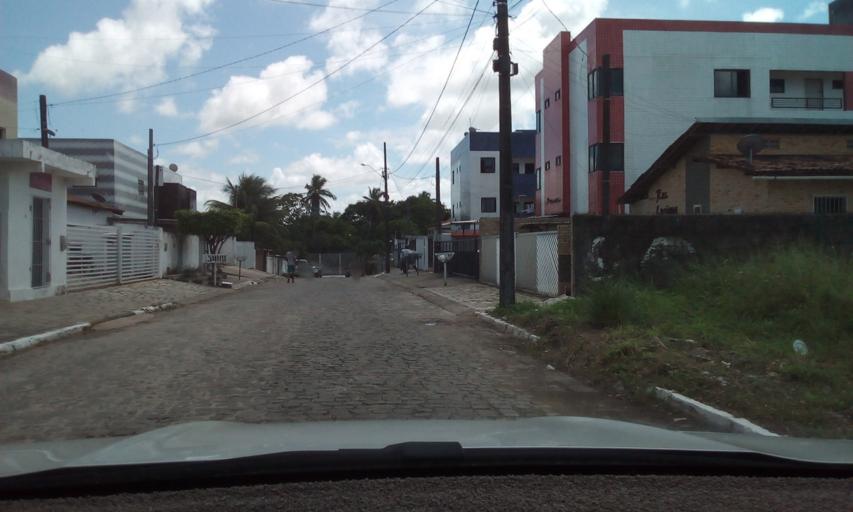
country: BR
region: Paraiba
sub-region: Joao Pessoa
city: Joao Pessoa
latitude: -7.1685
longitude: -34.8904
